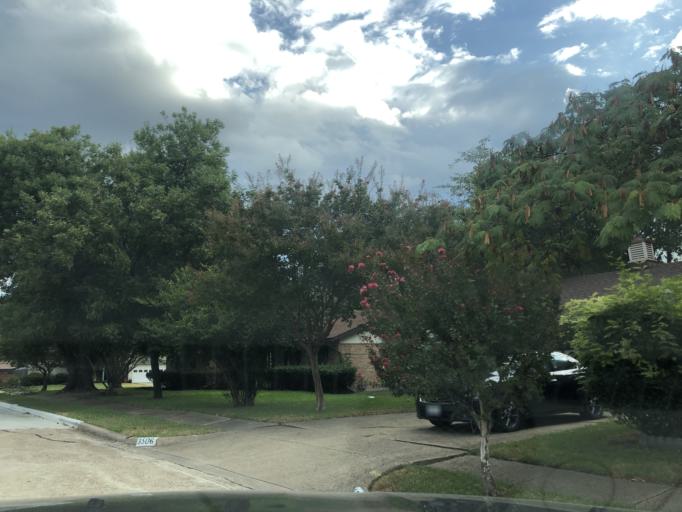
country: US
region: Texas
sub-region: Dallas County
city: Garland
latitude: 32.8732
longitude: -96.6500
